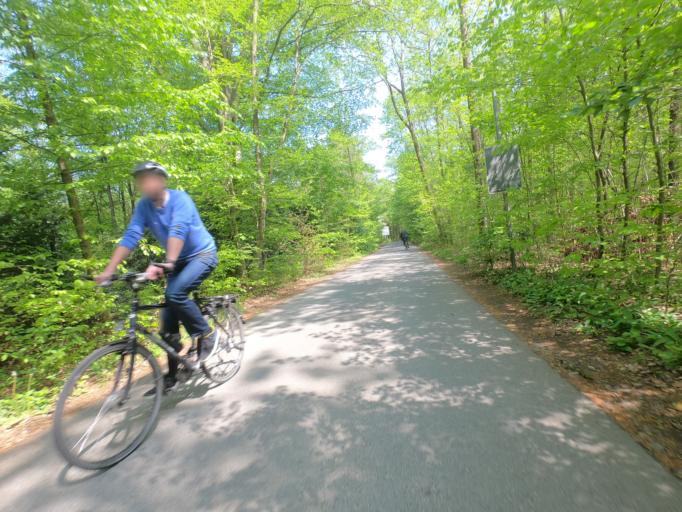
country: DE
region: Hesse
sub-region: Regierungsbezirk Darmstadt
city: Neu Isenburg
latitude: 50.0654
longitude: 8.6720
